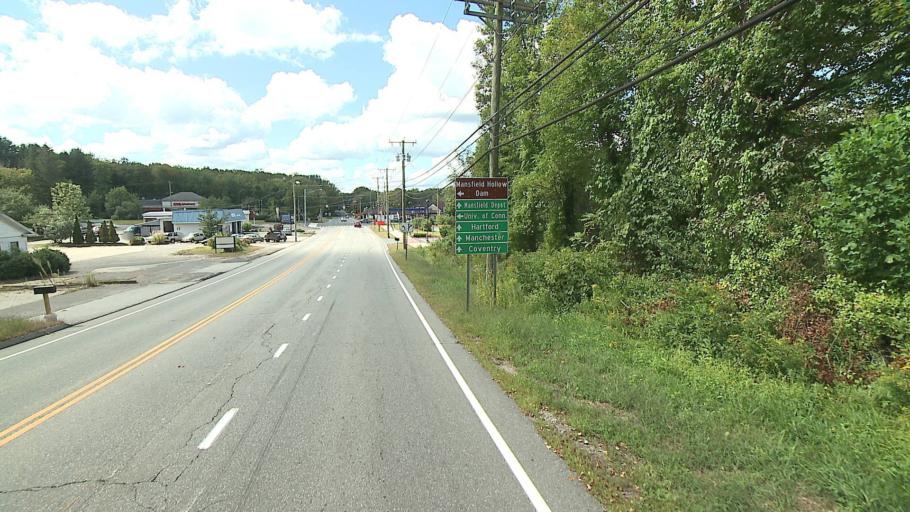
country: US
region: Connecticut
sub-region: Tolland County
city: Storrs
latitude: 41.8280
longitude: -72.2650
